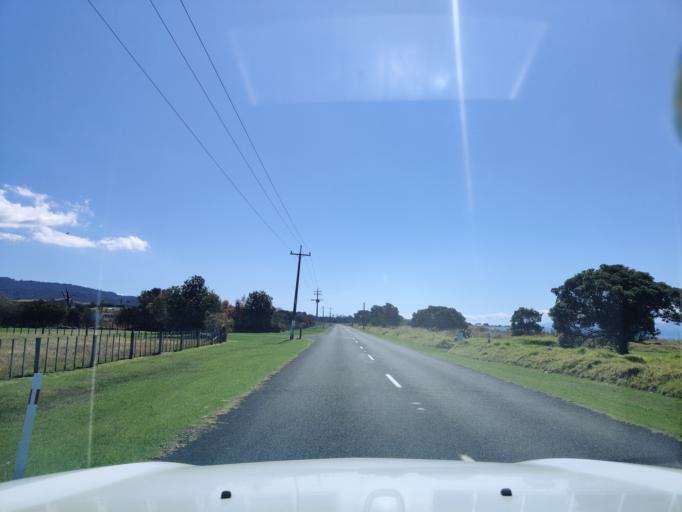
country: NZ
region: Waikato
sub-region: Thames-Coromandel District
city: Thames
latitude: -37.0739
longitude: 175.2959
